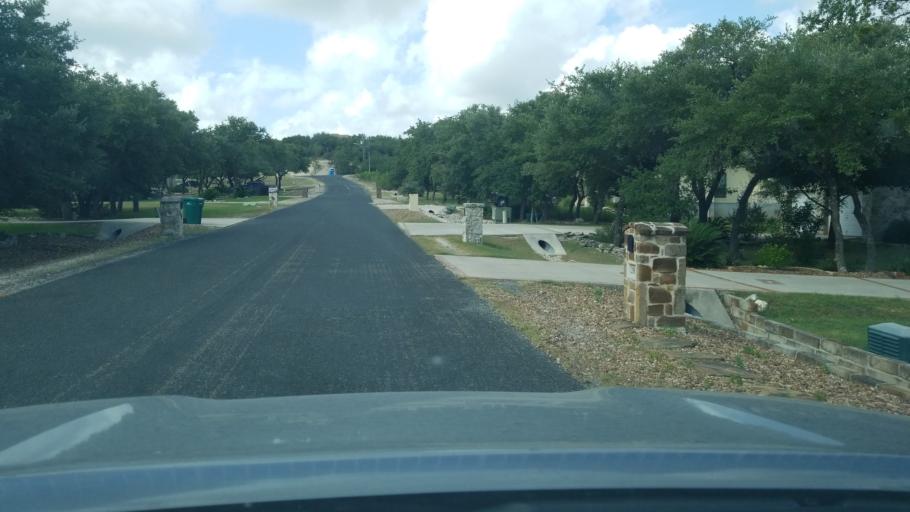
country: US
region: Texas
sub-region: Bexar County
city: Timberwood Park
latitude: 29.6910
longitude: -98.5107
